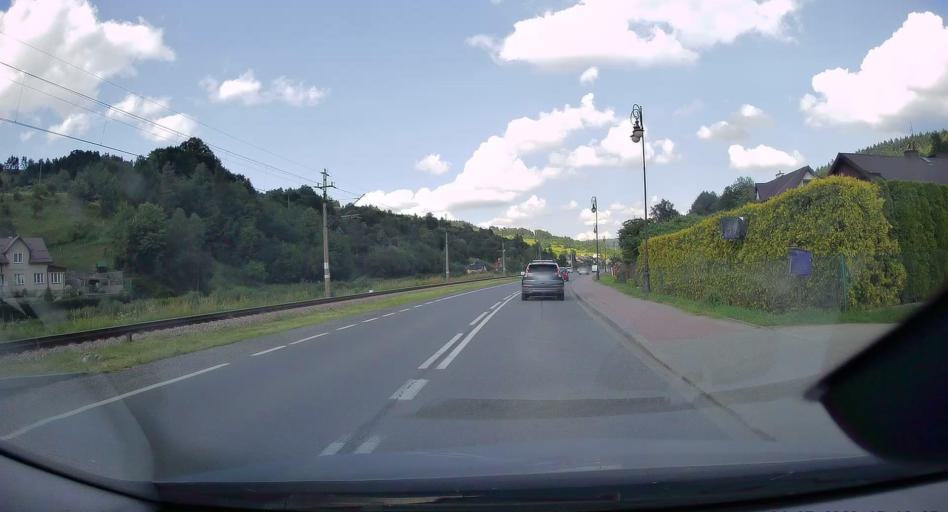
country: PL
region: Lesser Poland Voivodeship
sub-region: Powiat nowosadecki
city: Muszyna
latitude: 49.3616
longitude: 20.9170
